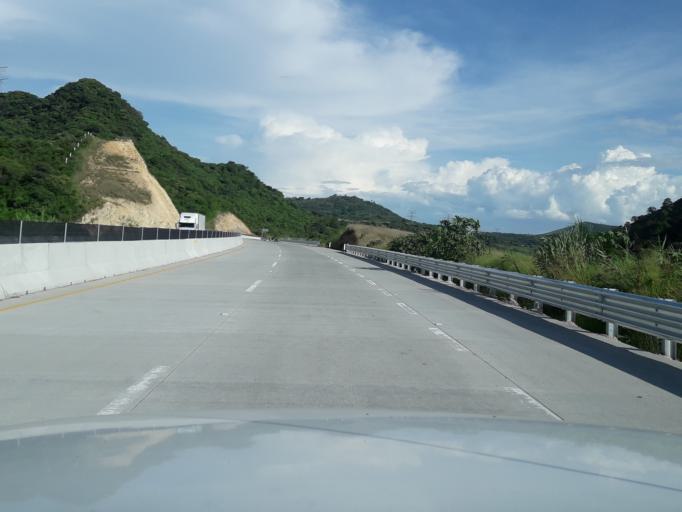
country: MX
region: Jalisco
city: Tala
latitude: 20.5990
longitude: -103.6756
